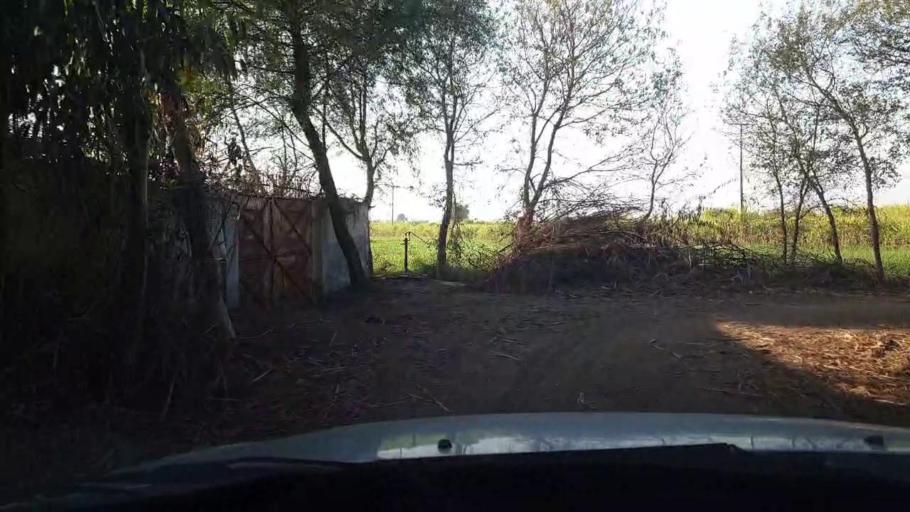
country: PK
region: Sindh
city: Mirpur Mathelo
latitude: 27.9880
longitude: 69.6281
